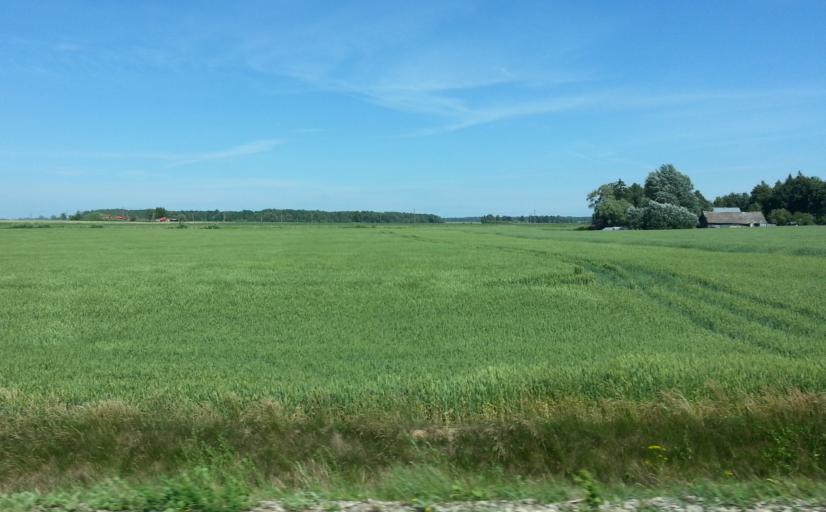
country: LT
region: Panevezys
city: Pasvalys
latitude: 56.1684
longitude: 24.4474
